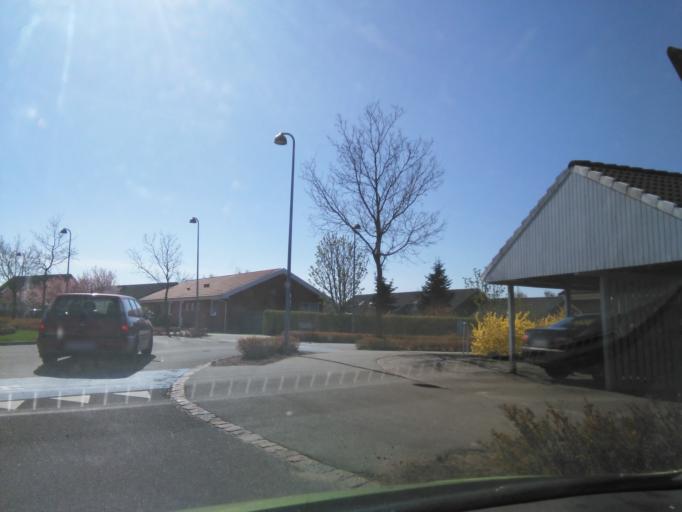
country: DK
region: South Denmark
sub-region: Billund Kommune
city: Billund
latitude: 55.7182
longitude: 9.1154
